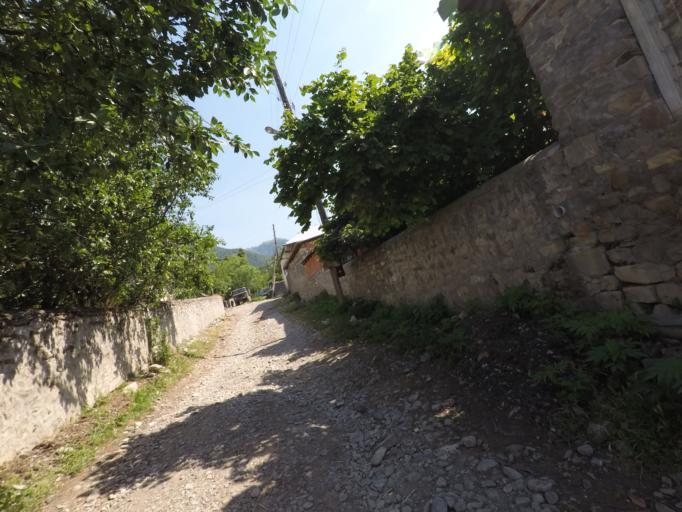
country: AZ
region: Qakh Rayon
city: Cinarli
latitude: 41.4848
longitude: 46.8502
